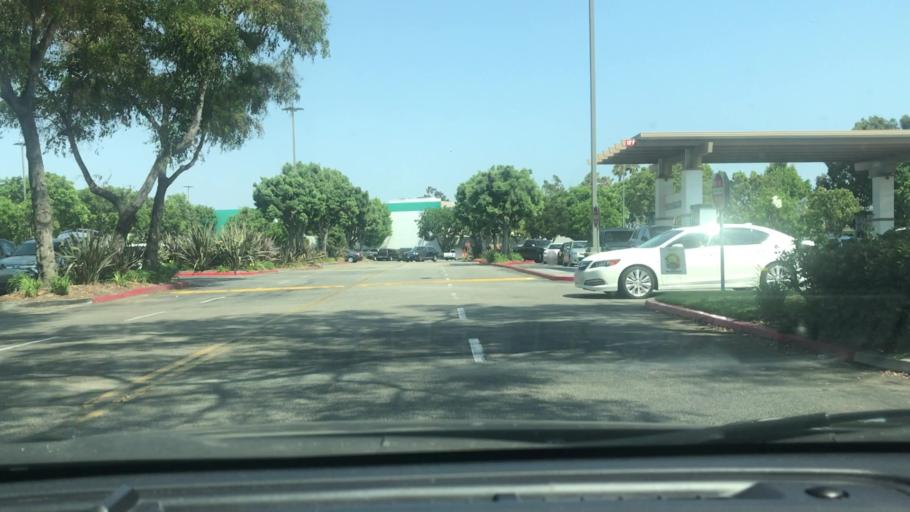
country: US
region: California
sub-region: Ventura County
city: El Rio
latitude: 34.2244
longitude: -119.1494
